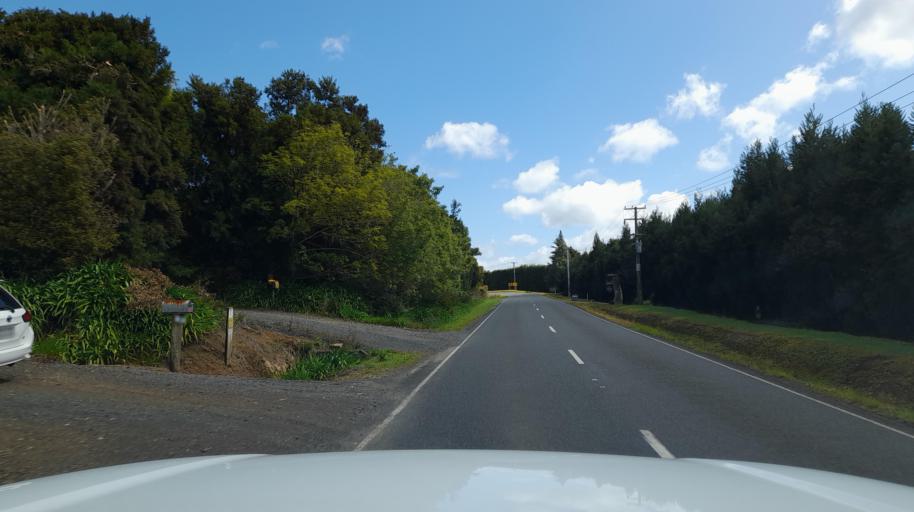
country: NZ
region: Northland
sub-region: Far North District
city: Kerikeri
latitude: -35.2327
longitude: 173.9065
